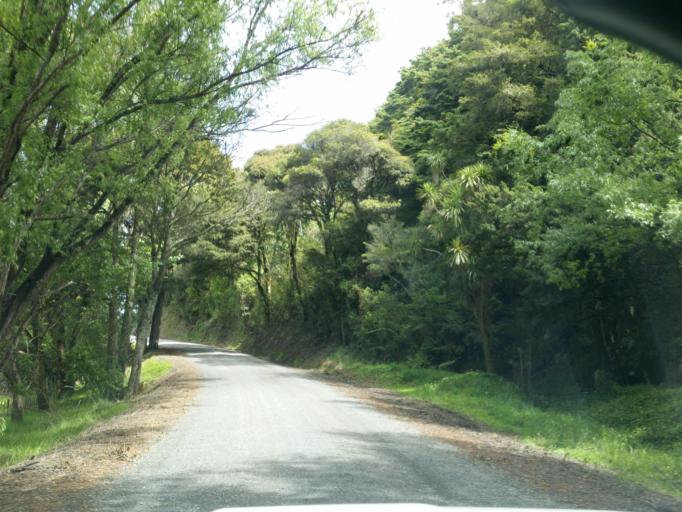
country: NZ
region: Northland
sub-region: Whangarei
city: Maungatapere
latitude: -35.9056
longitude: 174.1402
